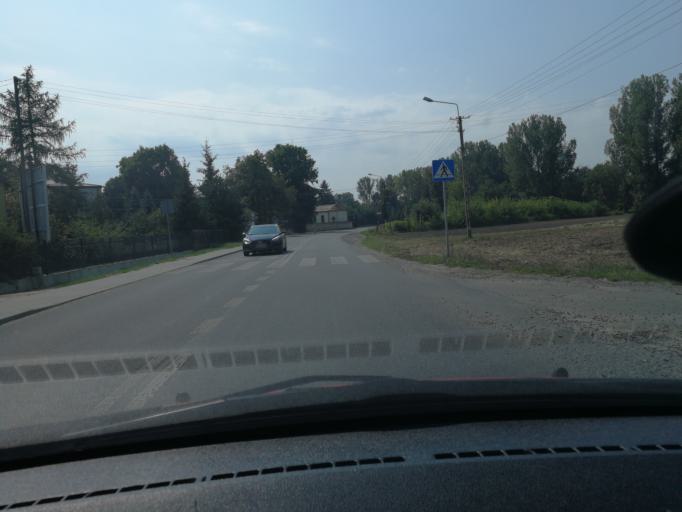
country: PL
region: Lodz Voivodeship
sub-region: powiat Lowicki
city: Bobrowniki
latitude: 52.0230
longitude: 20.0557
